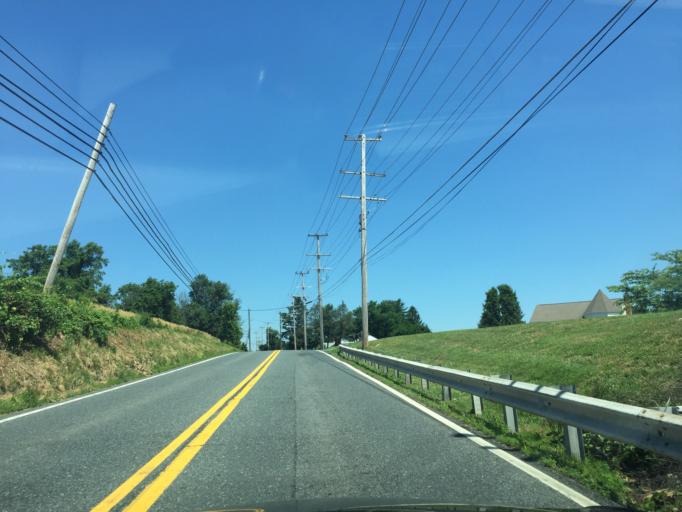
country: US
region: Maryland
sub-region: Harford County
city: Jarrettsville
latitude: 39.5973
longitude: -76.4759
